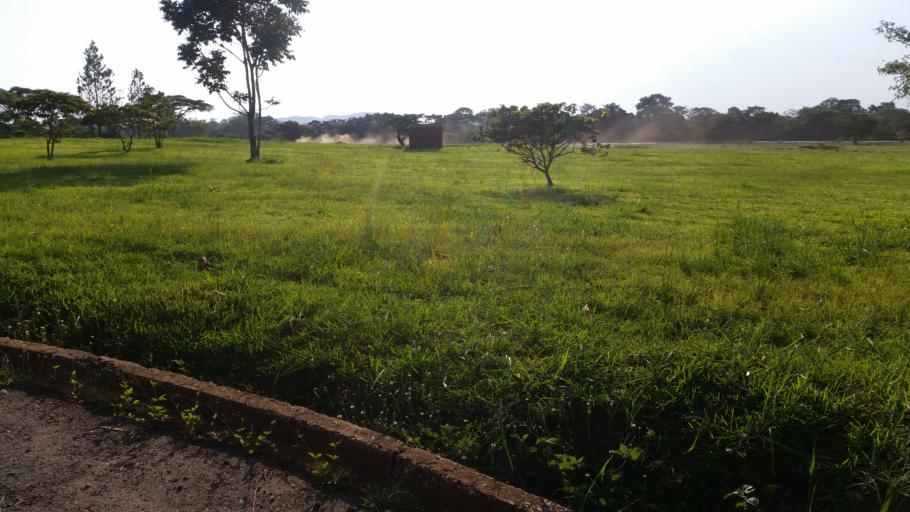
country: UG
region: Eastern Region
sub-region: Busia District
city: Busia
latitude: 0.5457
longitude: 34.0196
